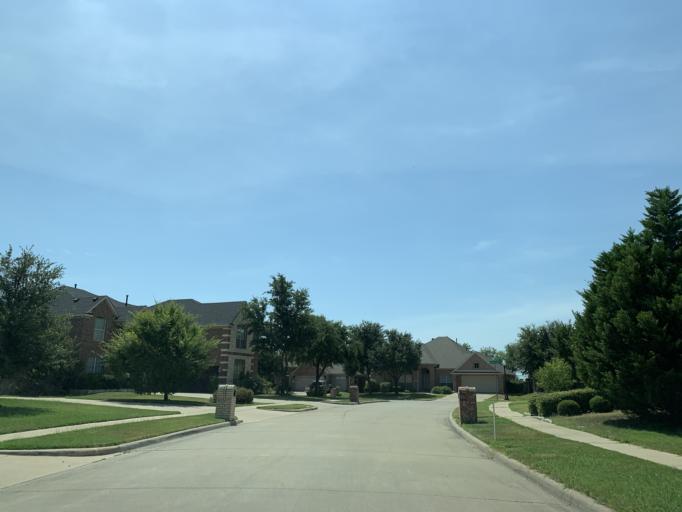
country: US
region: Texas
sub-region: Dallas County
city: Cedar Hill
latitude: 32.6403
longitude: -97.0462
